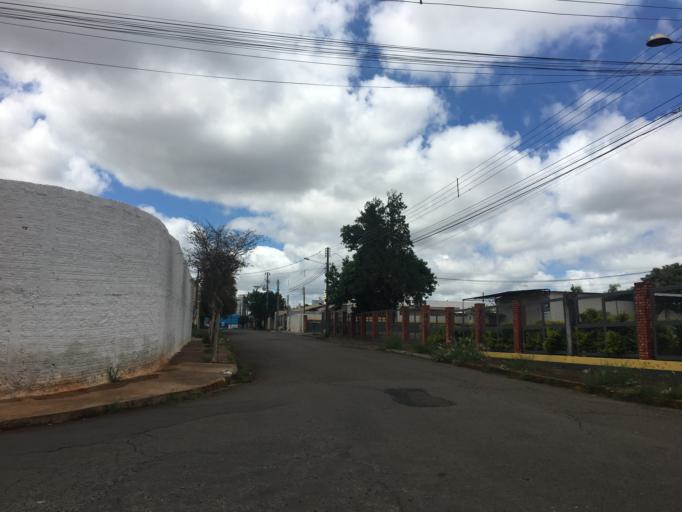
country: BR
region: Parana
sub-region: Londrina
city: Londrina
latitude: -23.2939
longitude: -51.1643
